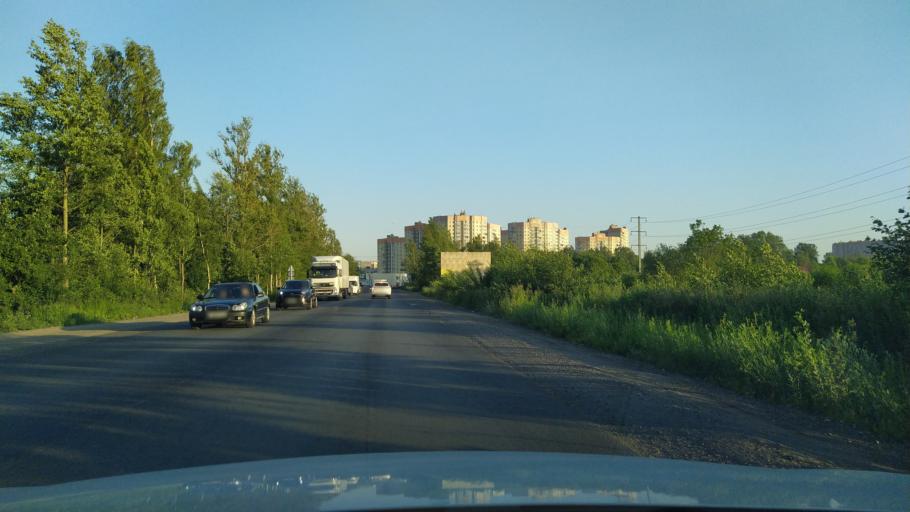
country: RU
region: Leningrad
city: Murino
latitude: 60.0521
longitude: 30.4656
